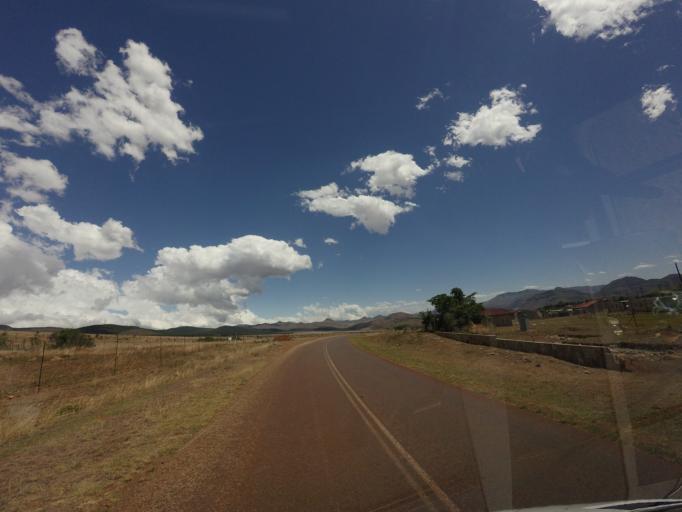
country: ZA
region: Mpumalanga
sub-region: Ehlanzeni District
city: Graksop
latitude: -24.6552
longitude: 30.8189
